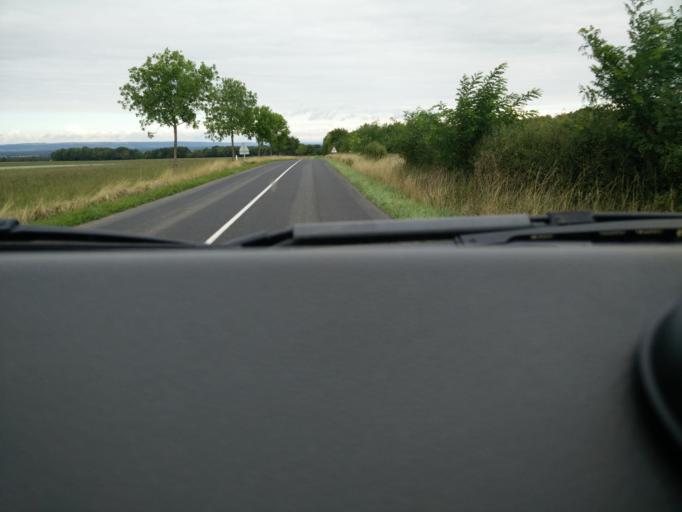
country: FR
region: Lorraine
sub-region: Departement de Meurthe-et-Moselle
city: Montauville
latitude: 48.9319
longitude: 5.8974
